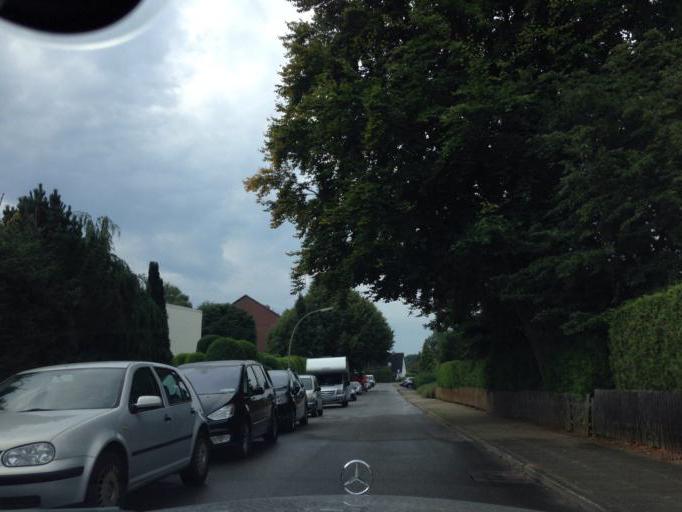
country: DE
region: Hamburg
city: Sasel
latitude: 53.6600
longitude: 10.1096
